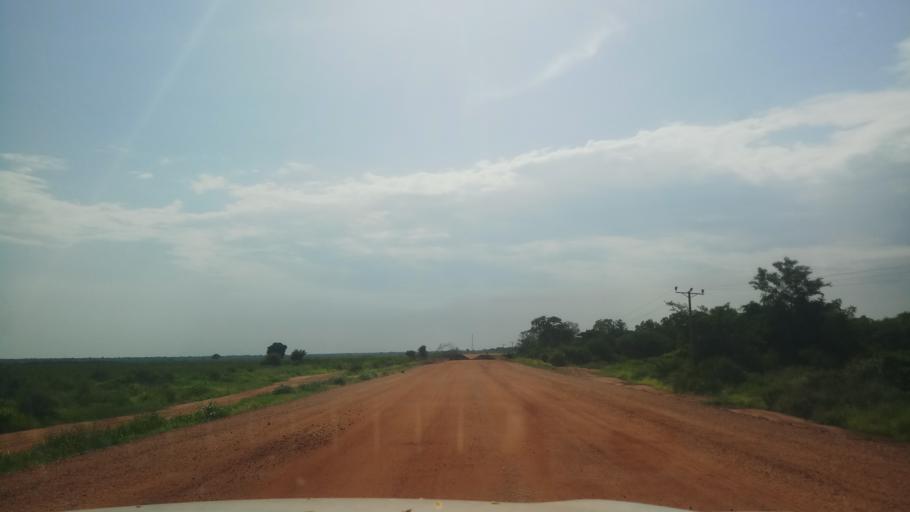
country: ET
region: Gambela
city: Gambela
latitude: 8.1443
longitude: 34.3641
